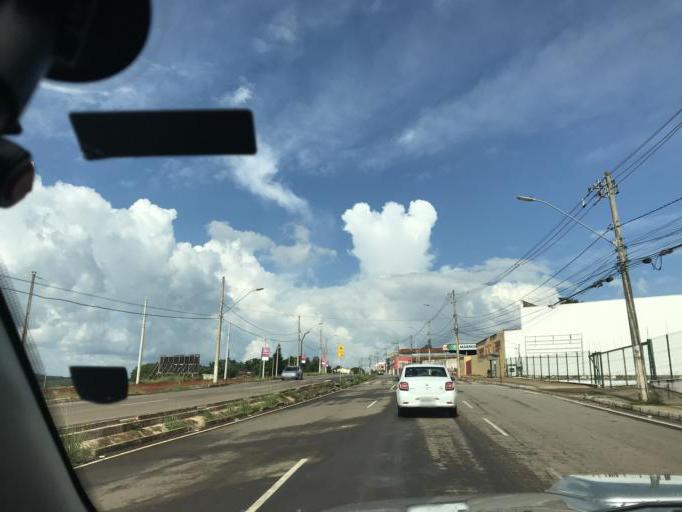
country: BR
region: Minas Gerais
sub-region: Tres Coracoes
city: Tres Coracoes
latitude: -21.6650
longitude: -45.2796
